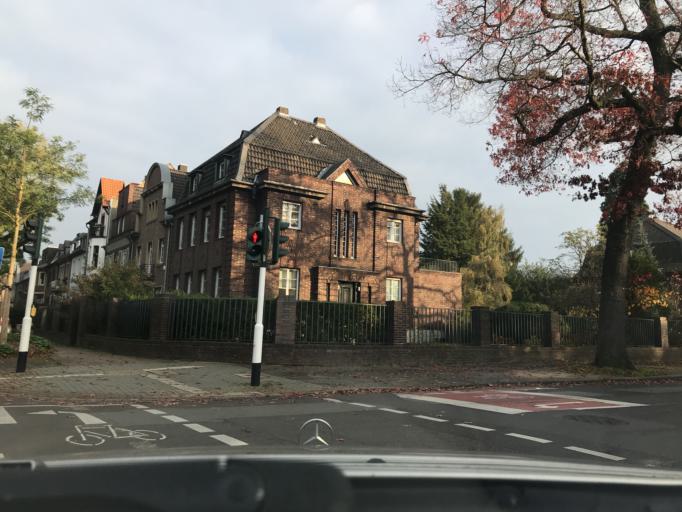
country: DE
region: North Rhine-Westphalia
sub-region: Regierungsbezirk Dusseldorf
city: Krefeld
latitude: 51.3408
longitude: 6.5791
